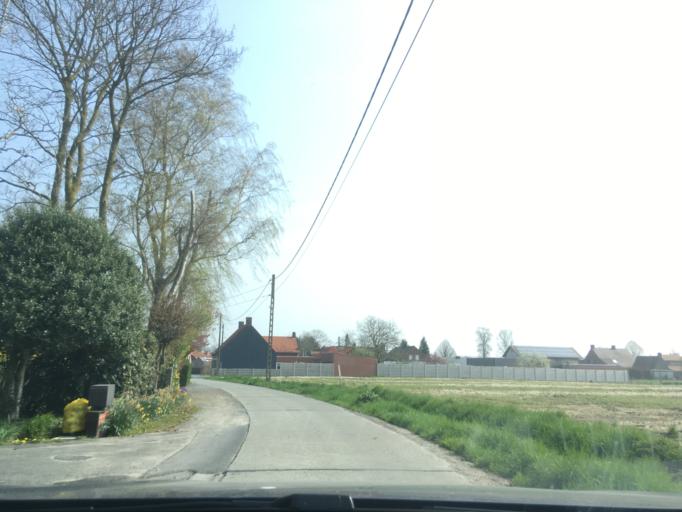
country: BE
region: Flanders
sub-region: Provincie West-Vlaanderen
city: Ardooie
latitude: 50.9796
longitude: 3.1883
